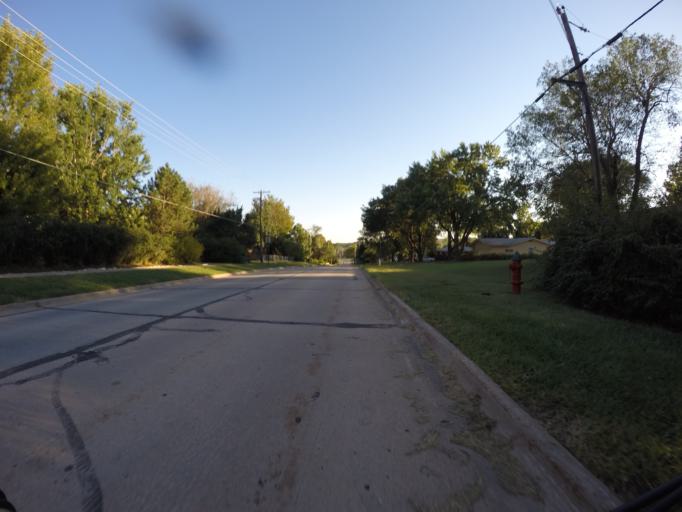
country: US
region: Kansas
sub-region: Riley County
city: Manhattan
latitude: 39.1922
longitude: -96.6261
